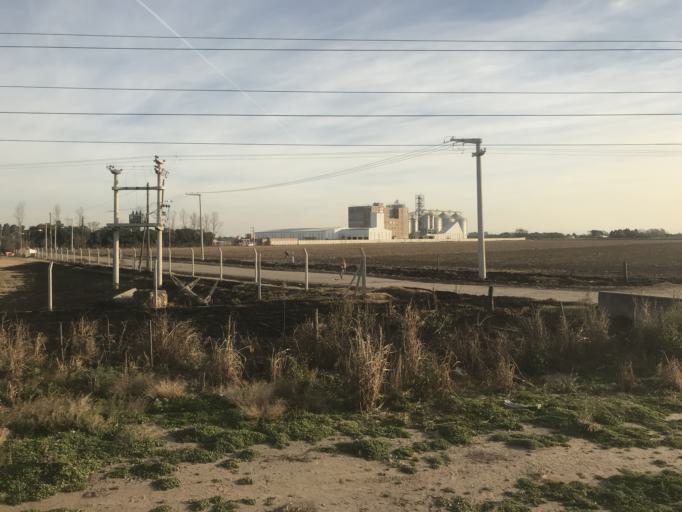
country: AR
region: Cordoba
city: Malvinas Argentinas
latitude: -31.4762
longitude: -64.0917
